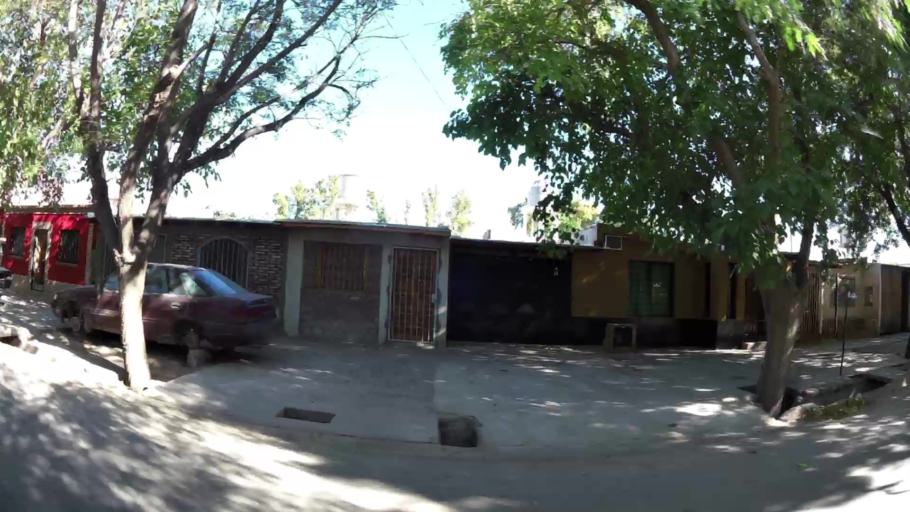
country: AR
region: Mendoza
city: Las Heras
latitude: -32.8317
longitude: -68.8321
